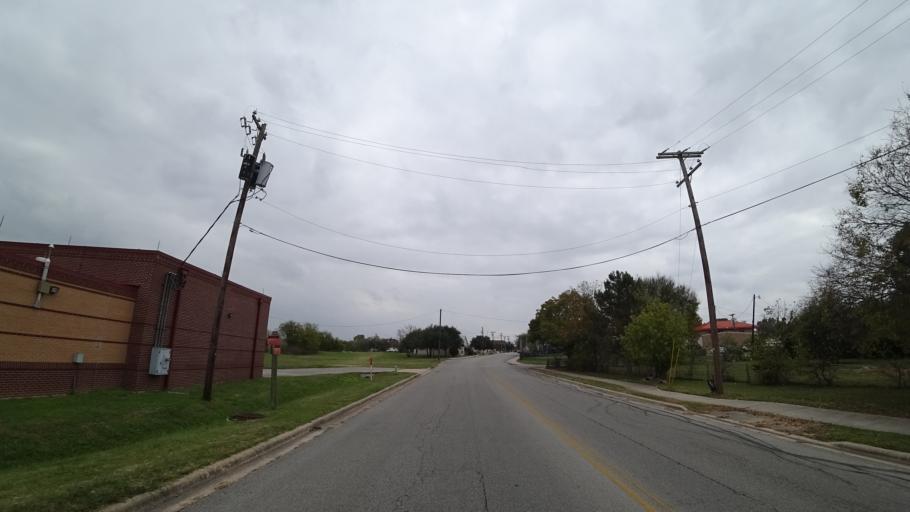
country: US
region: Texas
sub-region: Travis County
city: Pflugerville
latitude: 30.4417
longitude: -97.6188
